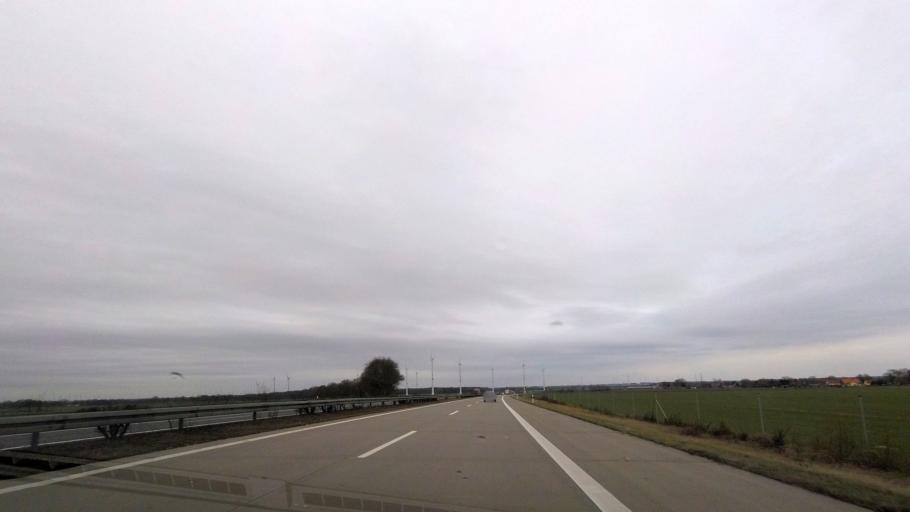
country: DE
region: Brandenburg
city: Heiligengrabe
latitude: 53.1757
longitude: 12.3141
